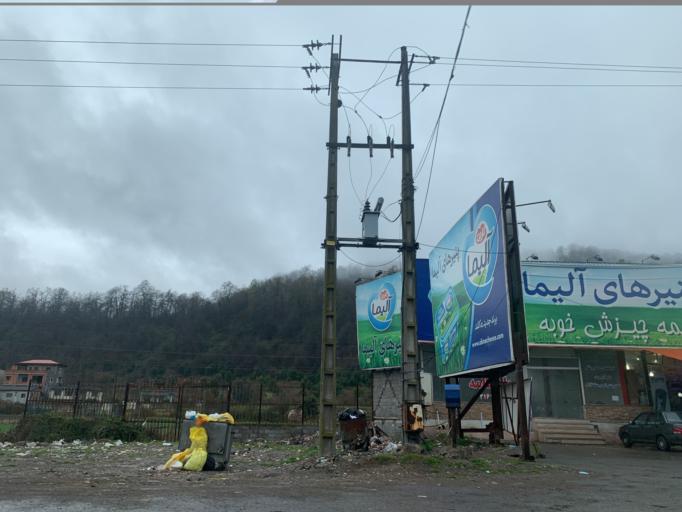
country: IR
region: Mazandaran
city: Amol
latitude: 36.3711
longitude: 52.3540
